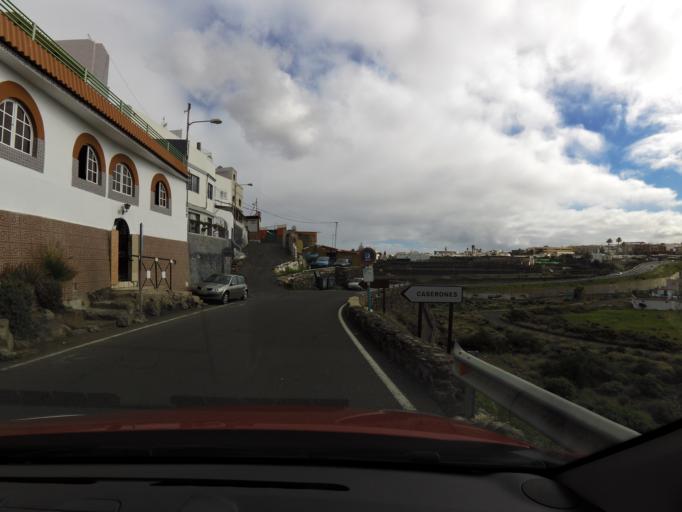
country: ES
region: Canary Islands
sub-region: Provincia de Las Palmas
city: Telde
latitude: 28.0060
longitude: -15.4212
